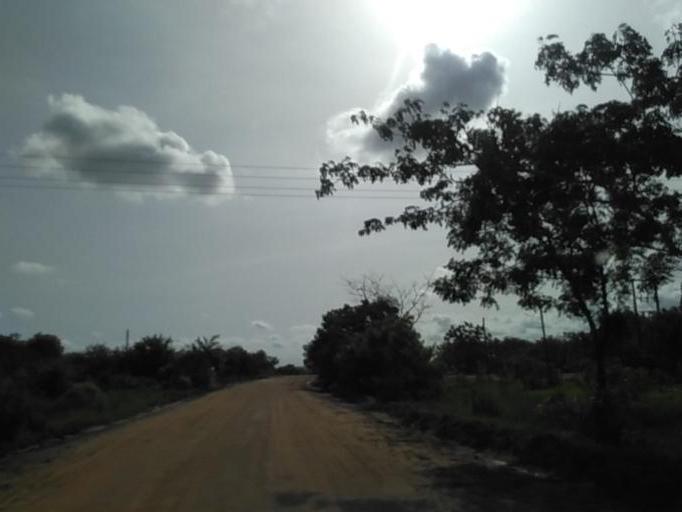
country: GH
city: Akropong
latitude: 6.0332
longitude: 0.3246
